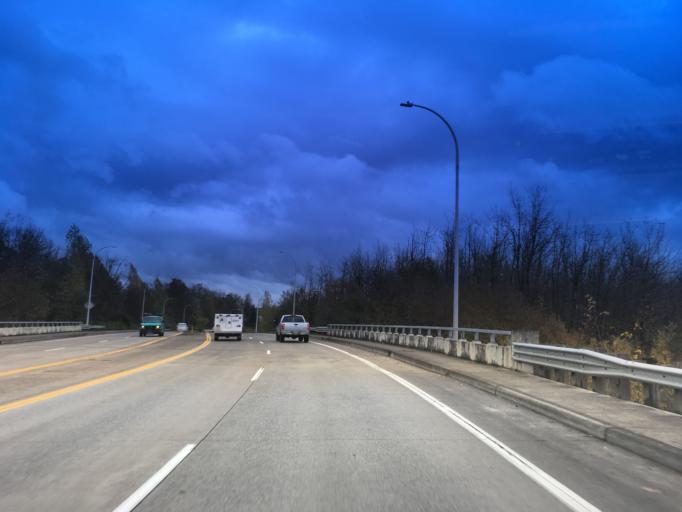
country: US
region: Oregon
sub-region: Multnomah County
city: Fairview
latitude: 45.5326
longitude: -122.4459
